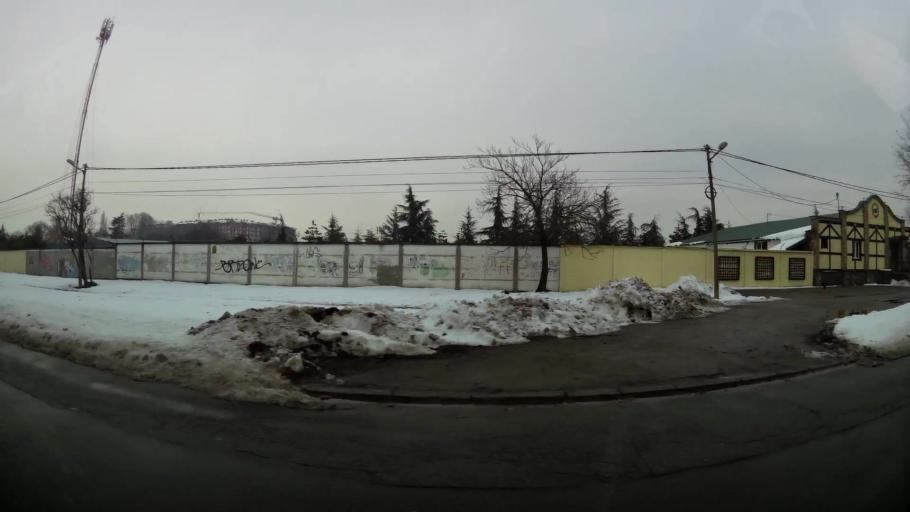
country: RS
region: Central Serbia
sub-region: Belgrade
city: Zemun
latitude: 44.8525
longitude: 20.3789
